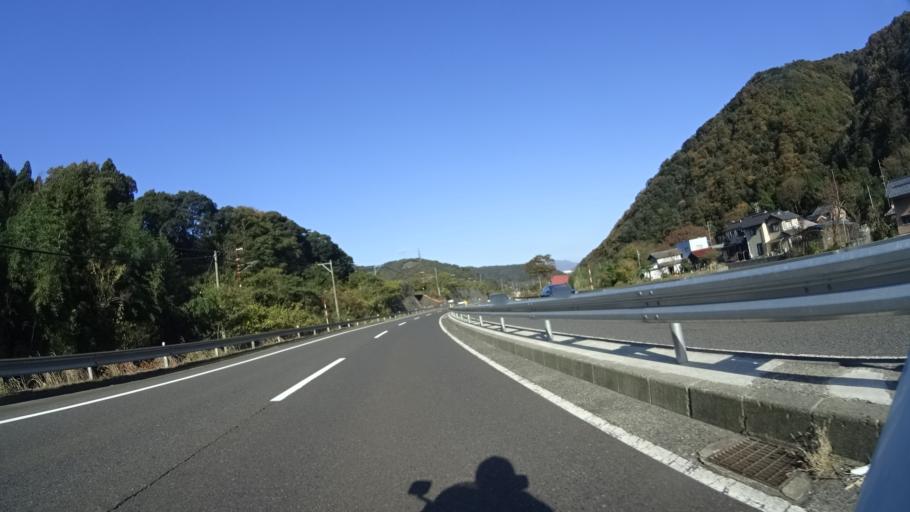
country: JP
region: Fukui
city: Tsuruga
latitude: 35.6063
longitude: 136.0894
